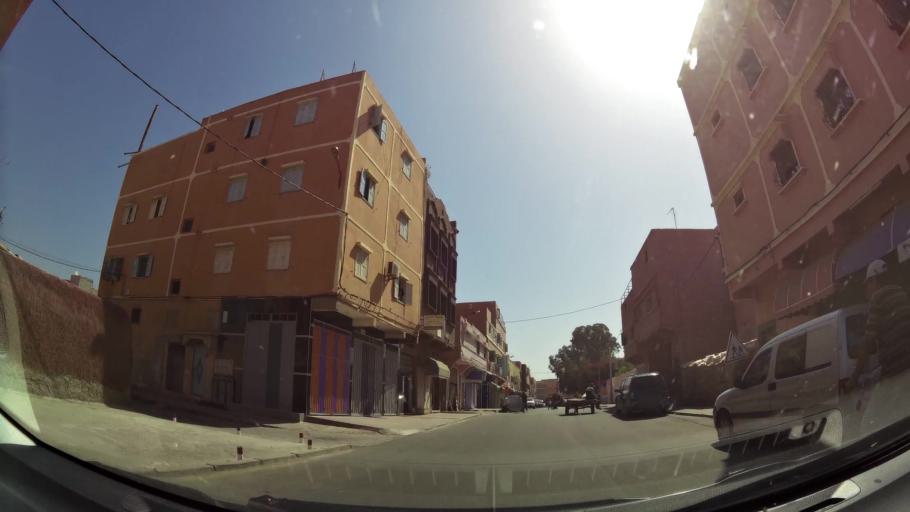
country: MA
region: Souss-Massa-Draa
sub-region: Inezgane-Ait Mellou
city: Inezgane
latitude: 30.3458
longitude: -9.5051
